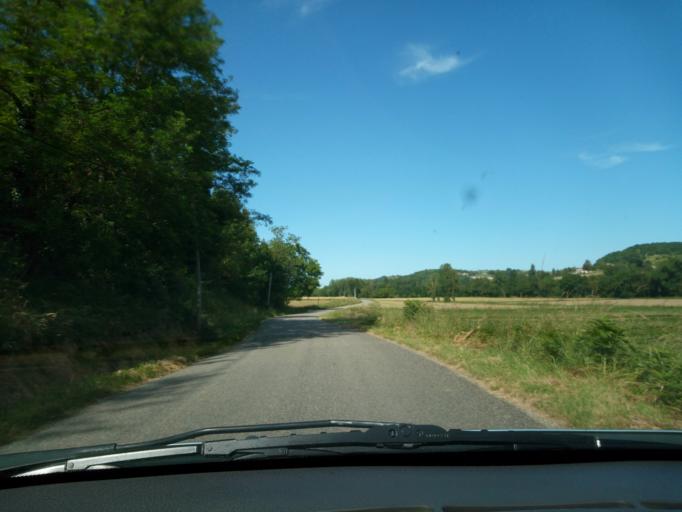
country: FR
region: Midi-Pyrenees
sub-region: Departement du Lot
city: Castelnau-Montratier
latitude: 44.2351
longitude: 1.3334
